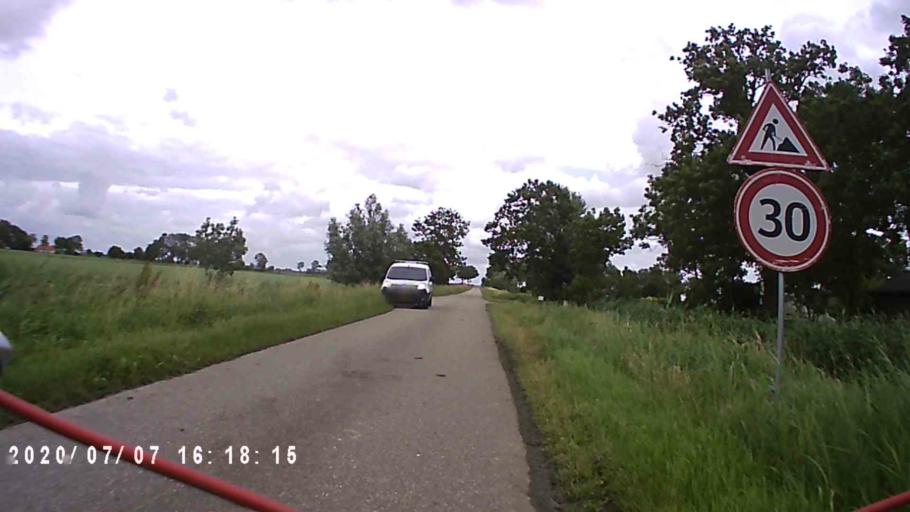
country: NL
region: Groningen
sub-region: Gemeente Winsum
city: Winsum
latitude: 53.3704
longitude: 6.5669
